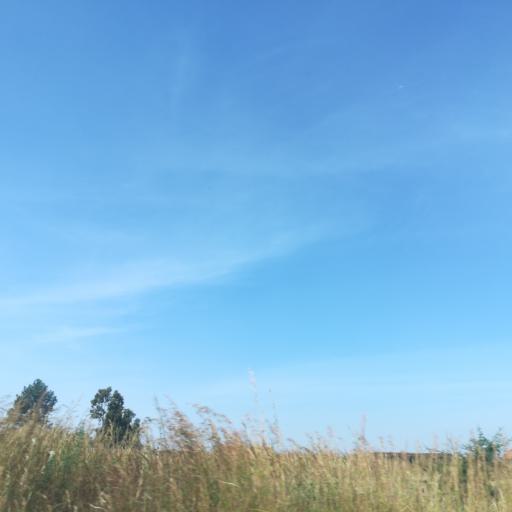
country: NG
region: Plateau
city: Bukuru
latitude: 9.7653
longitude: 8.8880
